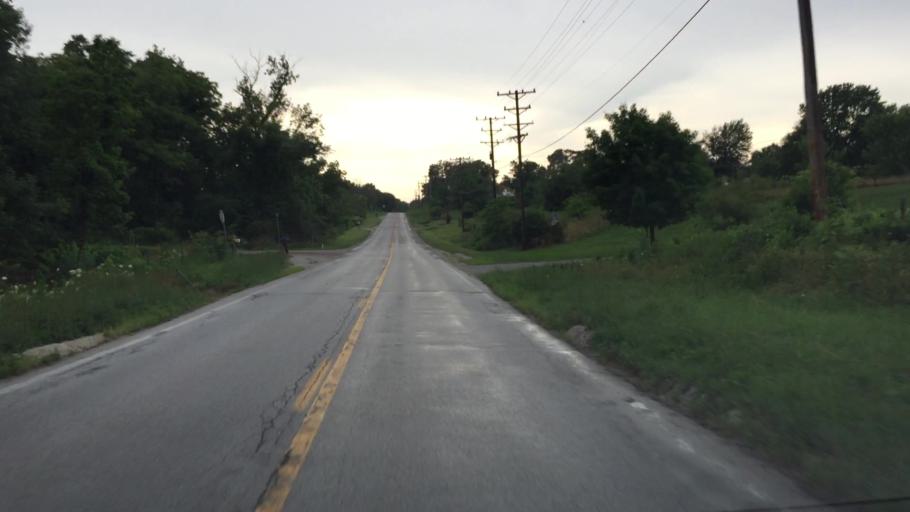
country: US
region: Illinois
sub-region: Hancock County
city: Warsaw
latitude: 40.3565
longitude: -91.4163
